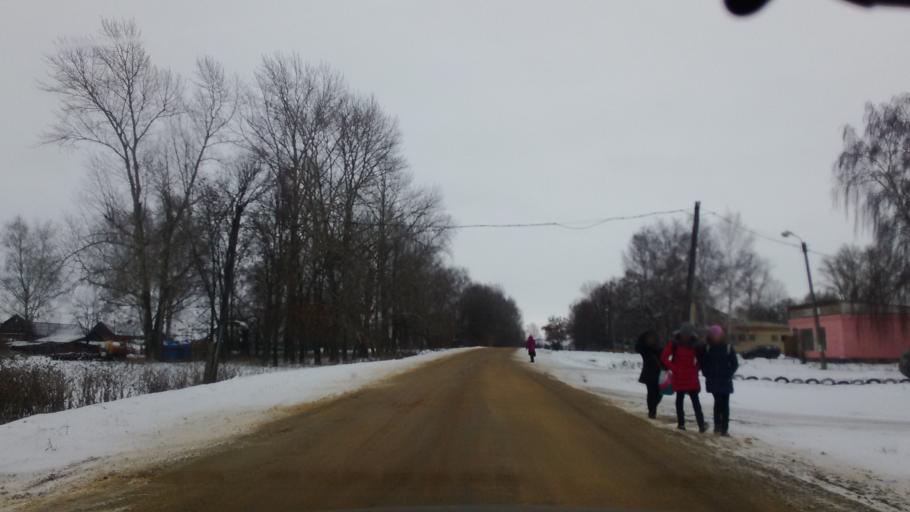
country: RU
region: Tula
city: Bogoroditsk
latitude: 53.7629
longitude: 37.9872
